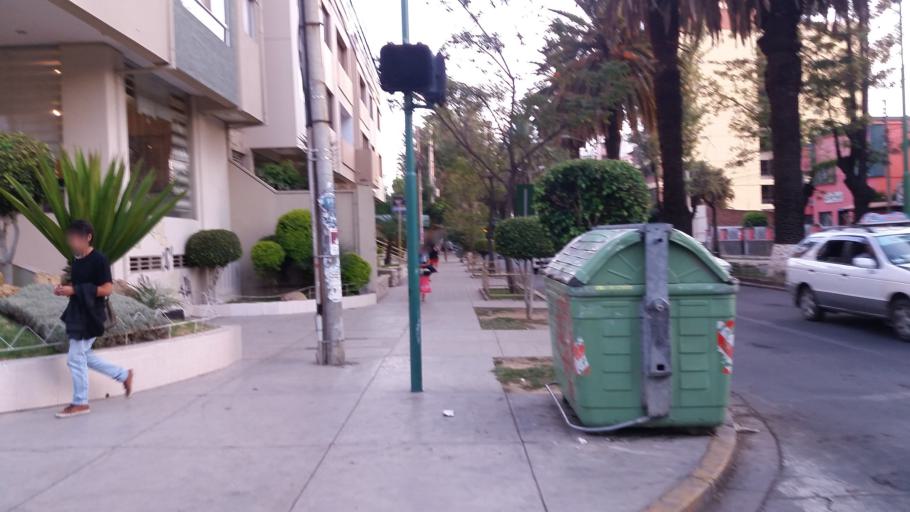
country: BO
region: Cochabamba
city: Cochabamba
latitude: -17.3861
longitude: -66.1601
